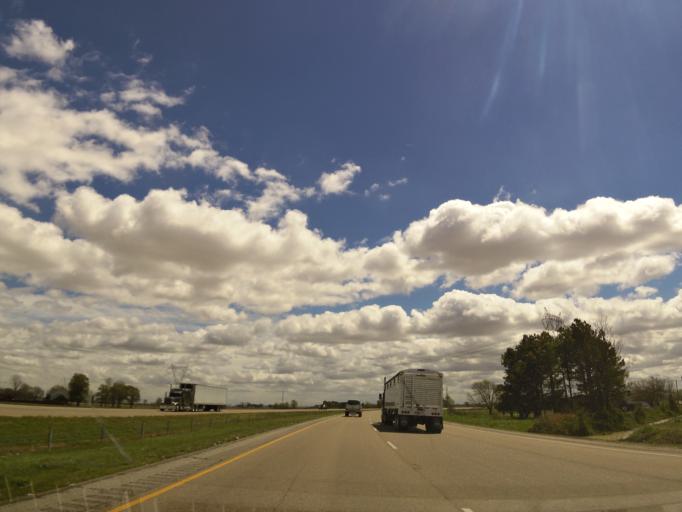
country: US
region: Arkansas
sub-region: Craighead County
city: Bay
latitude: 35.7718
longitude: -90.5805
